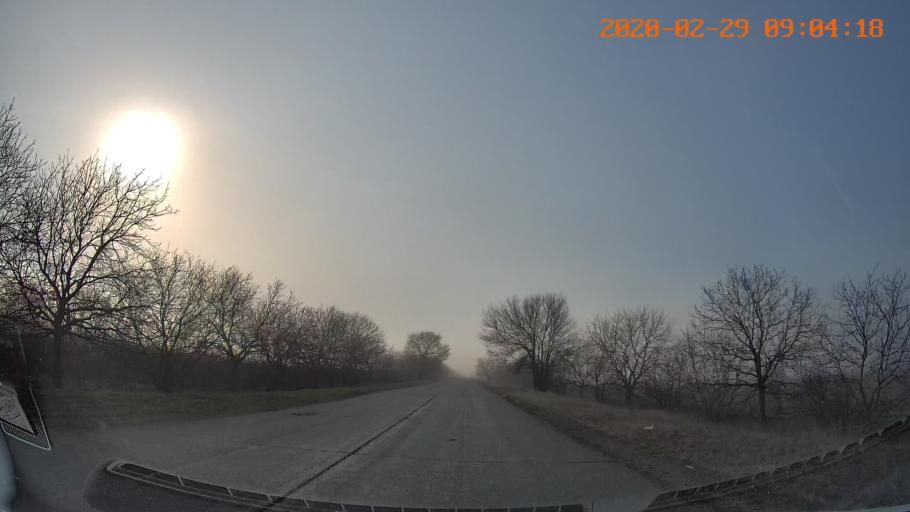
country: MD
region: Telenesti
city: Tiraspolul Nou
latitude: 46.9043
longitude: 29.7355
